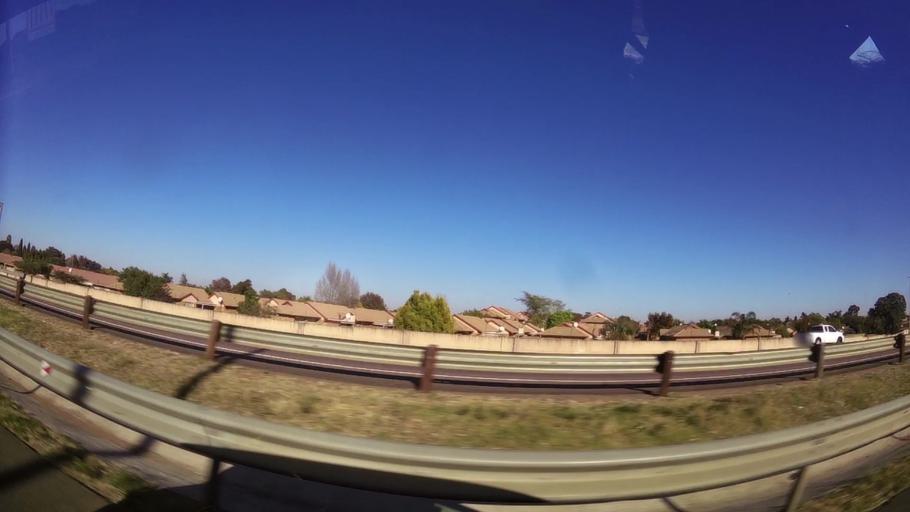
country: ZA
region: Gauteng
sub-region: City of Tshwane Metropolitan Municipality
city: Centurion
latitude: -25.8325
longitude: 28.2452
